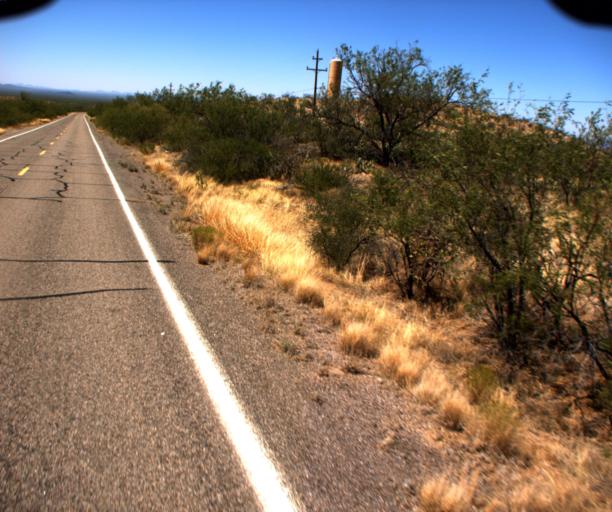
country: US
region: Arizona
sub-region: Pima County
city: Three Points
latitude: 32.0034
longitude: -111.5724
